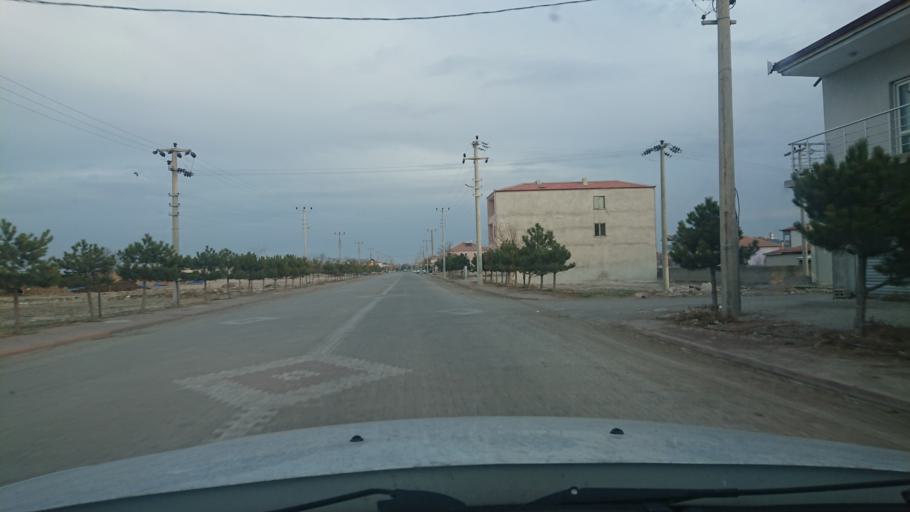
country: TR
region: Aksaray
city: Yesilova
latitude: 38.3358
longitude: 33.7513
